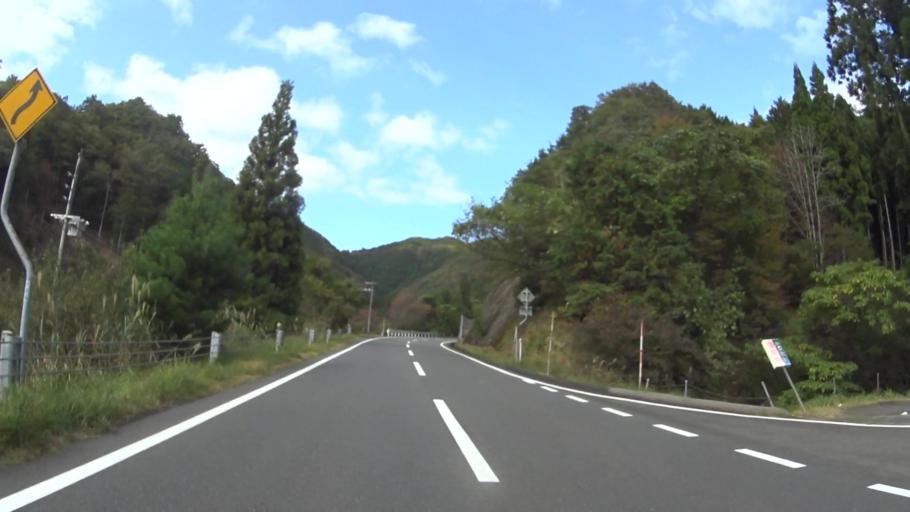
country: JP
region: Hyogo
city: Toyooka
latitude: 35.5185
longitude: 134.9898
